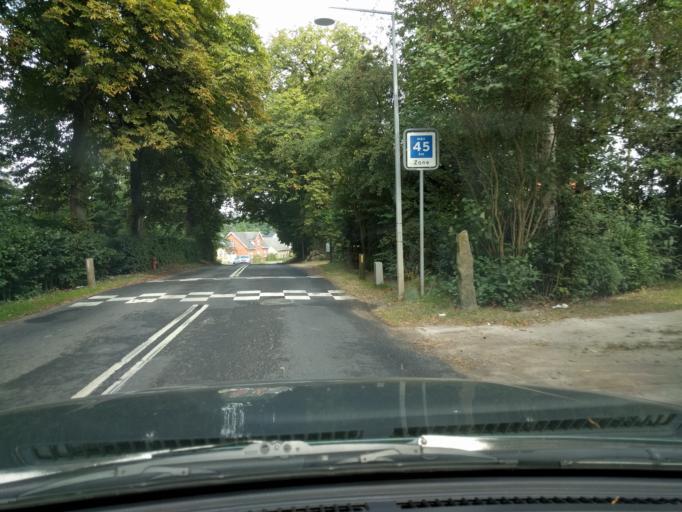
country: DK
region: South Denmark
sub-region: Odense Kommune
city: Bullerup
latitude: 55.3967
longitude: 10.4615
